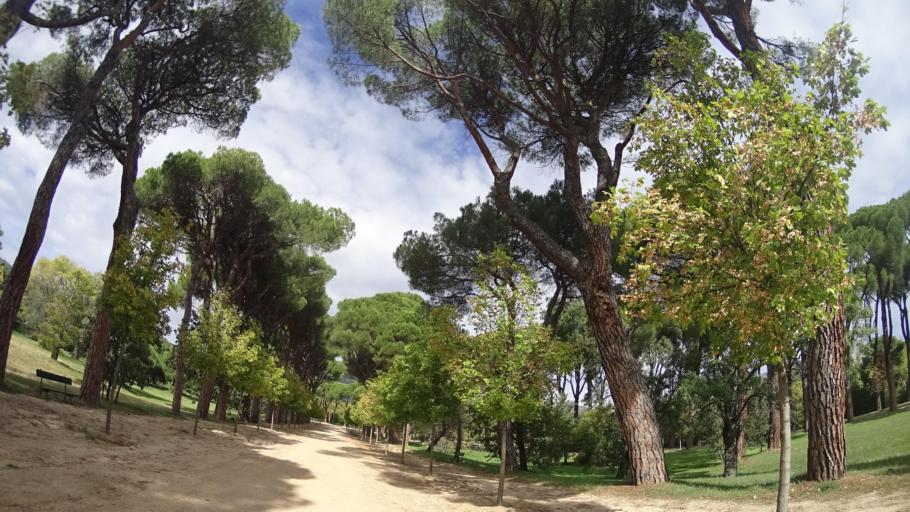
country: ES
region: Madrid
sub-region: Provincia de Madrid
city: San Lorenzo de El Escorial
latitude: 40.5863
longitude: -4.1400
